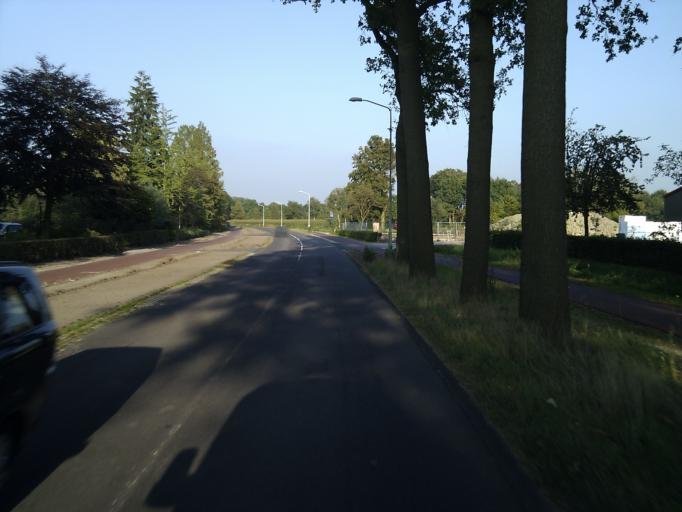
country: NL
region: North Brabant
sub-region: Gemeente Best
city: Best
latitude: 51.5315
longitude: 5.4152
